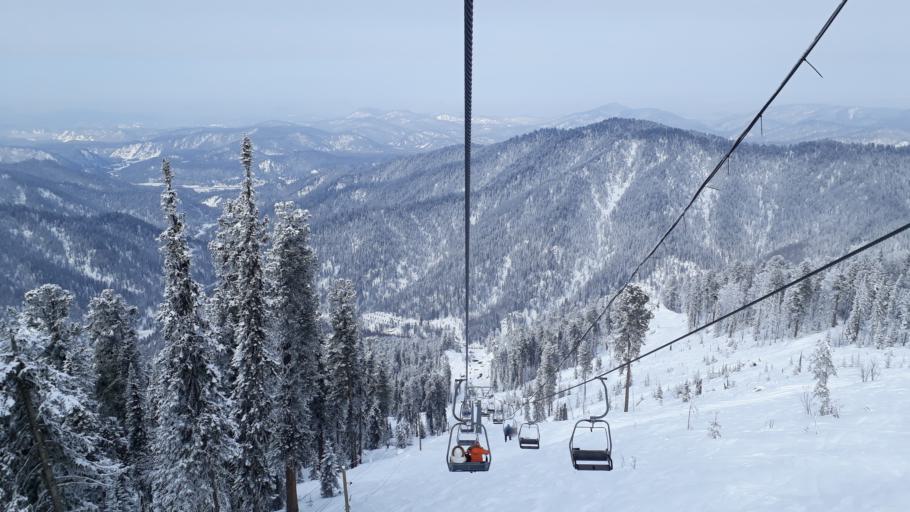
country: RU
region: Altay
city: Iogach
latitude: 51.7306
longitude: 87.3003
